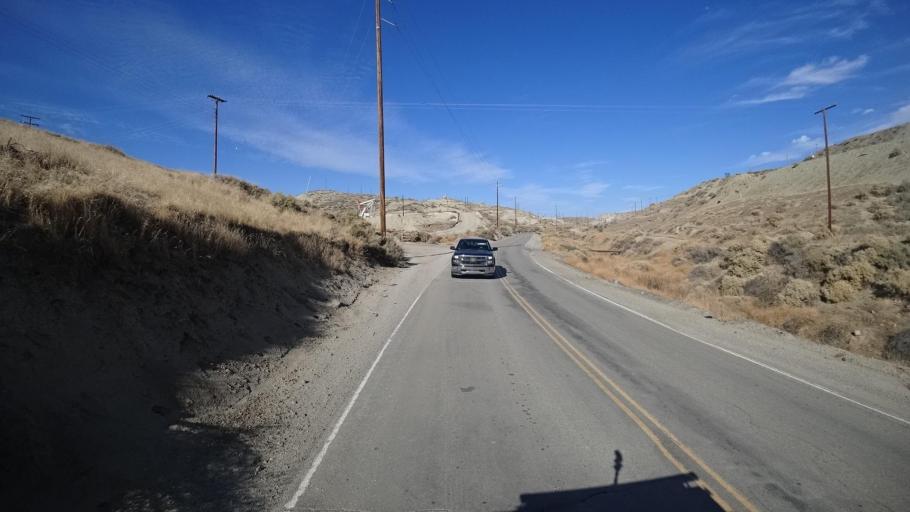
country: US
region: California
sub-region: Kern County
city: Oildale
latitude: 35.5764
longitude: -118.9606
